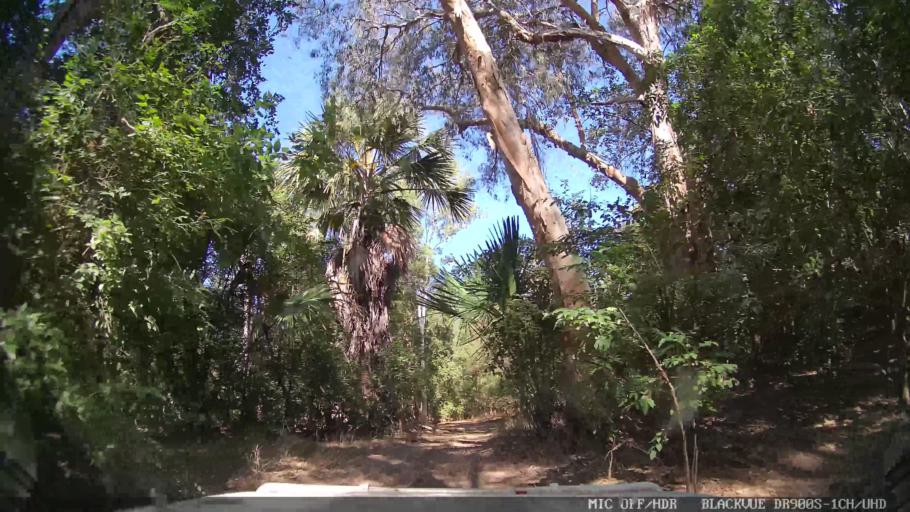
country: AU
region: Queensland
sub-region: Cook
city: Cooktown
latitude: -15.1970
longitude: 144.4293
